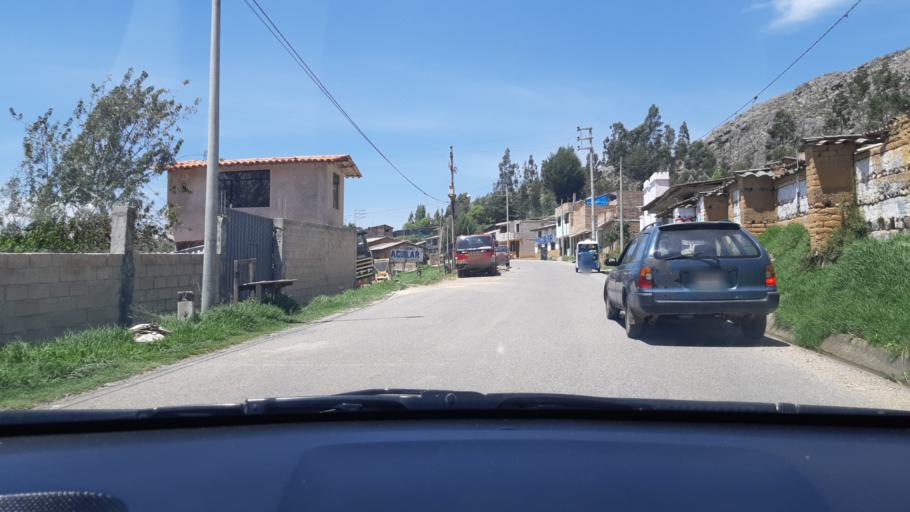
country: PE
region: Cajamarca
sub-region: Provincia de Cajamarca
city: Llacanora
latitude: -7.1774
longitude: -78.4569
